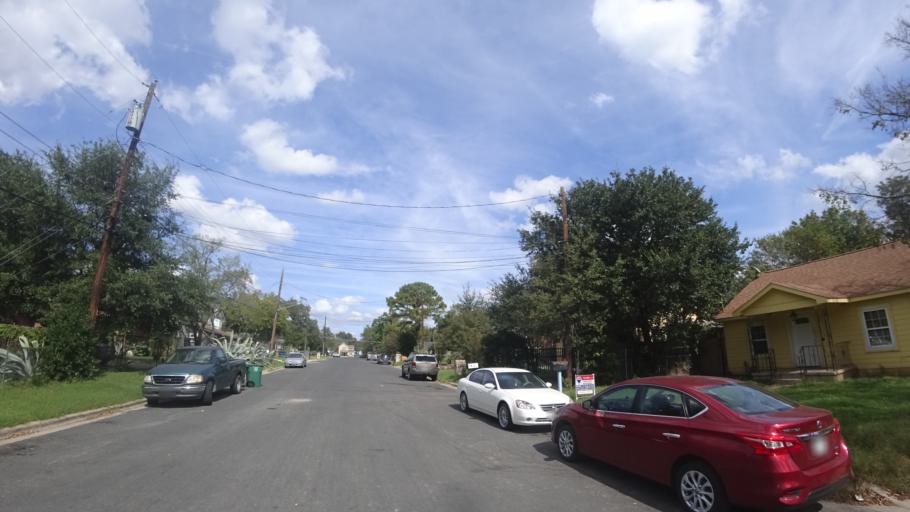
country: US
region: Texas
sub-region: Travis County
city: Austin
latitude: 30.2636
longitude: -97.7045
